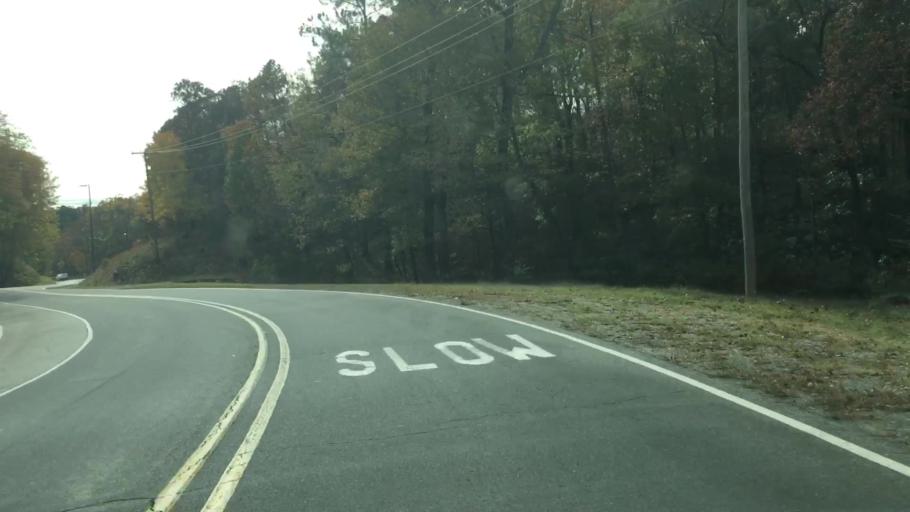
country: US
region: Arkansas
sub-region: Pulaski County
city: North Little Rock
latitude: 34.8173
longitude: -92.2897
